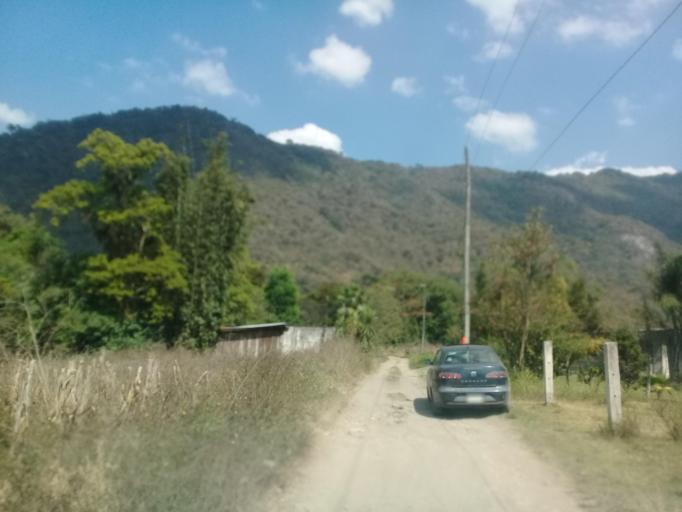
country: MX
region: Veracruz
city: Jalapilla
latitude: 18.8290
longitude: -97.0718
